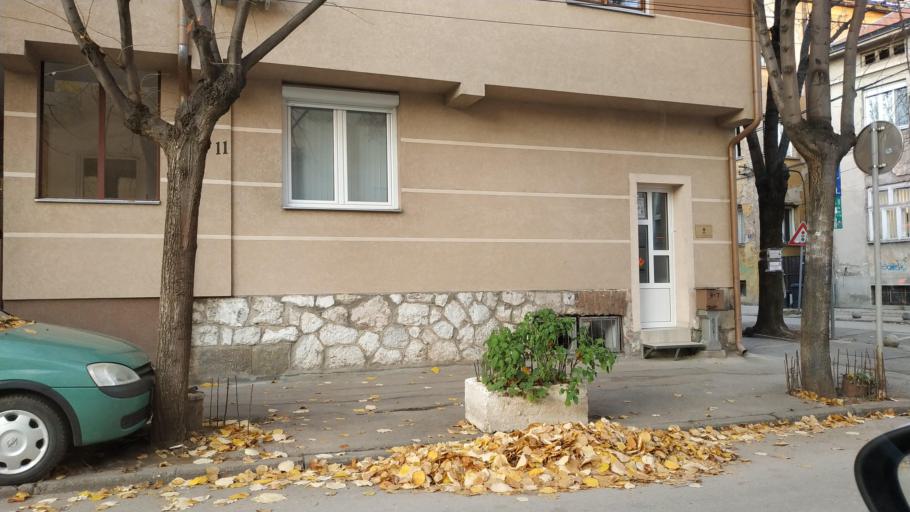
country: RS
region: Central Serbia
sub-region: Nisavski Okrug
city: Nis
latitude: 43.3193
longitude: 21.9030
